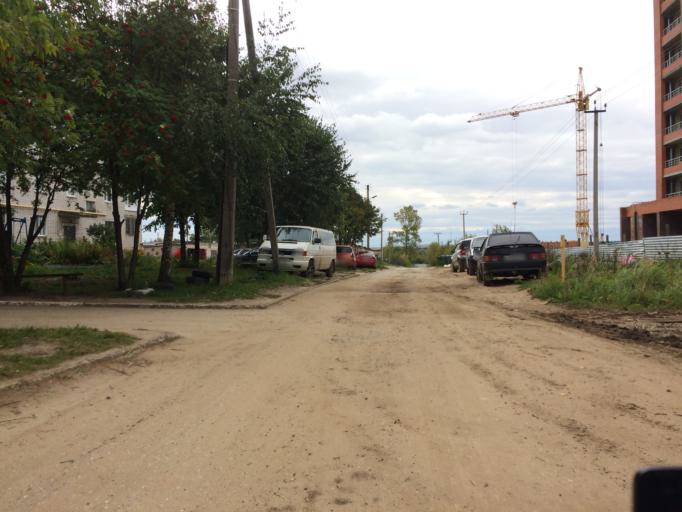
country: RU
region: Mariy-El
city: Yoshkar-Ola
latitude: 56.6535
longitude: 47.9696
